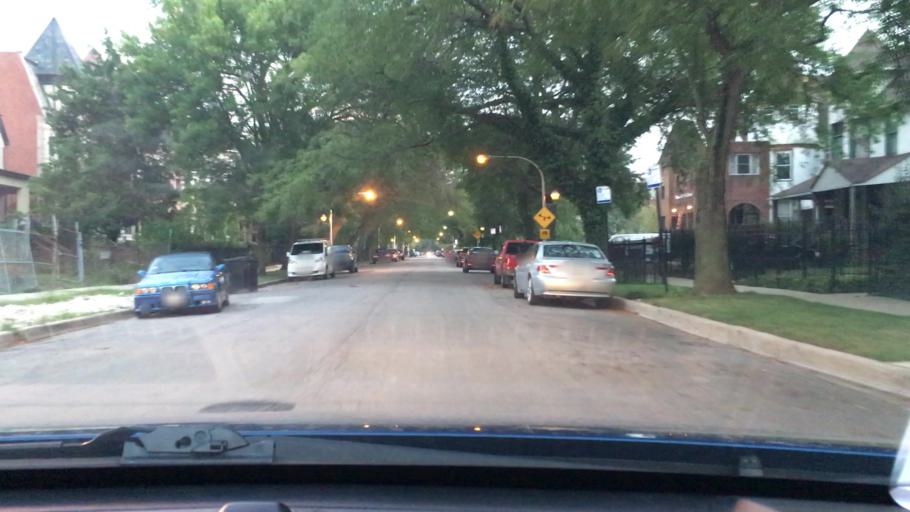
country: US
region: Illinois
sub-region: Cook County
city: Chicago
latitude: 41.8129
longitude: -87.5993
